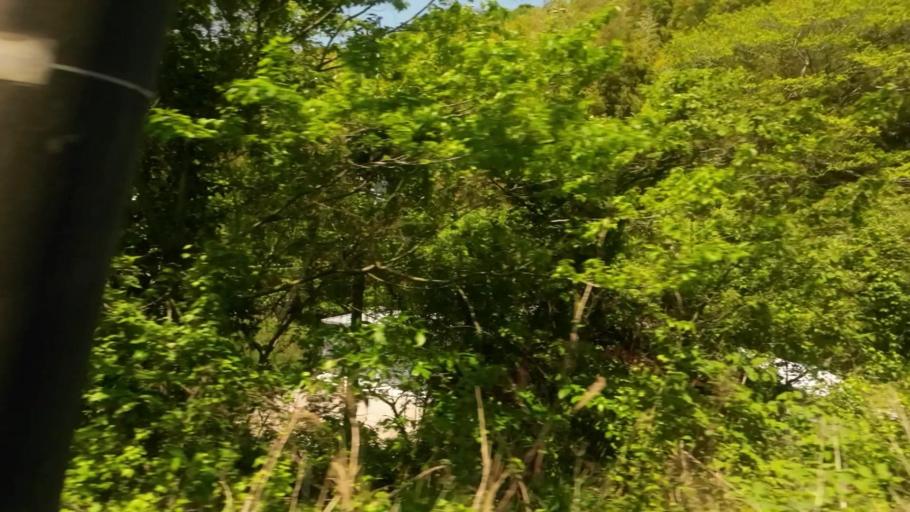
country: JP
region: Ehime
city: Hojo
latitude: 33.9934
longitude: 132.7761
